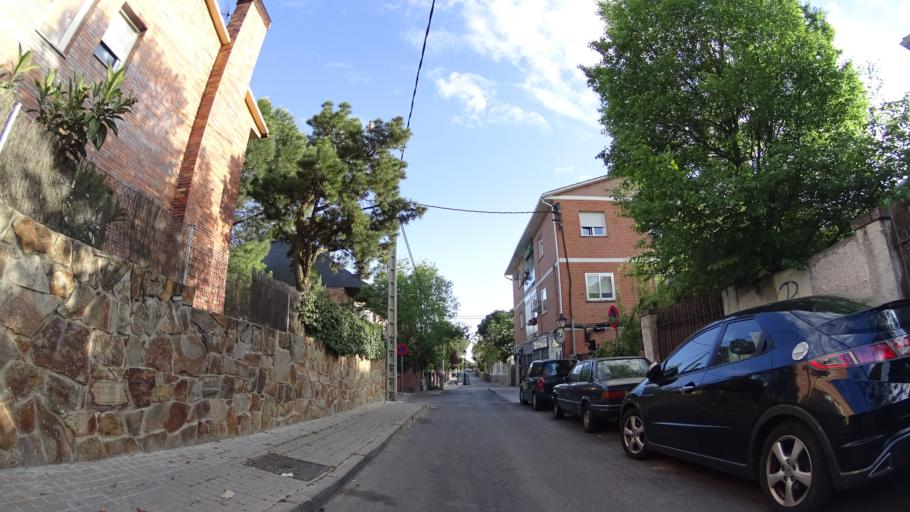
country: ES
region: Madrid
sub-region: Provincia de Madrid
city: Torrelodones
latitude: 40.5775
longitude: -3.9554
